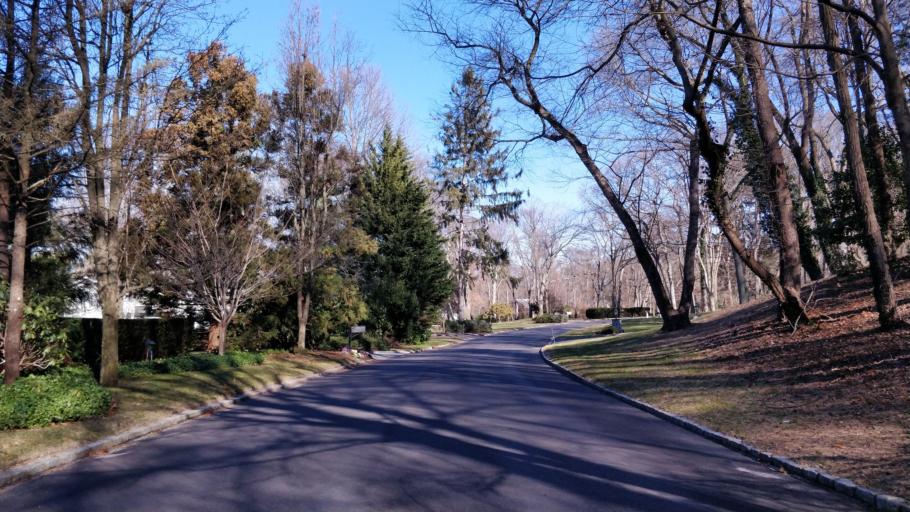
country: US
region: New York
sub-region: Nassau County
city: Brookville
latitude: 40.8120
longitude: -73.5824
